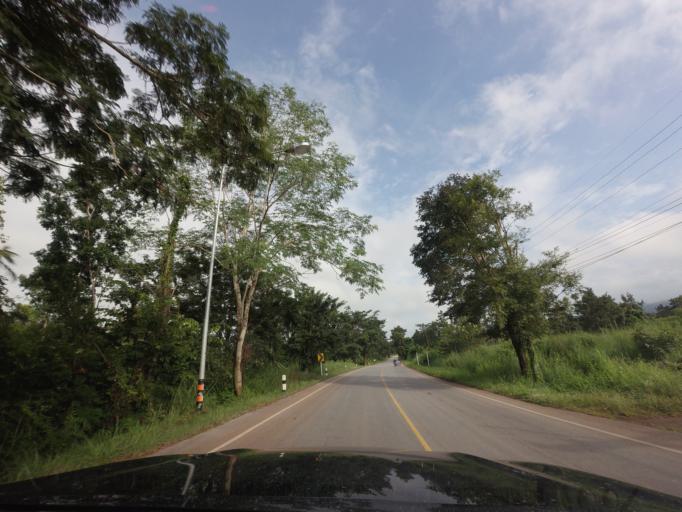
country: TH
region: Changwat Udon Thani
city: Nam Som
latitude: 17.8390
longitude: 102.2575
